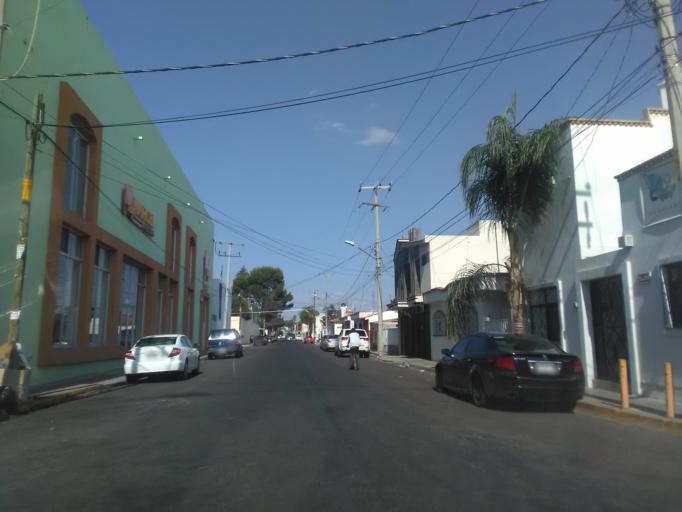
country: MX
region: Durango
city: Victoria de Durango
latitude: 24.0313
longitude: -104.6487
